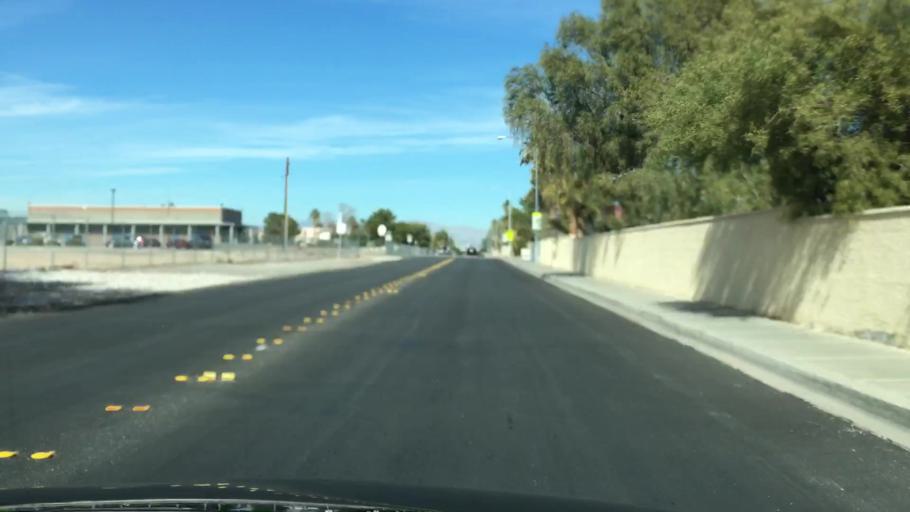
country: US
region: Nevada
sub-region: Clark County
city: Paradise
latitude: 36.0524
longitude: -115.1498
